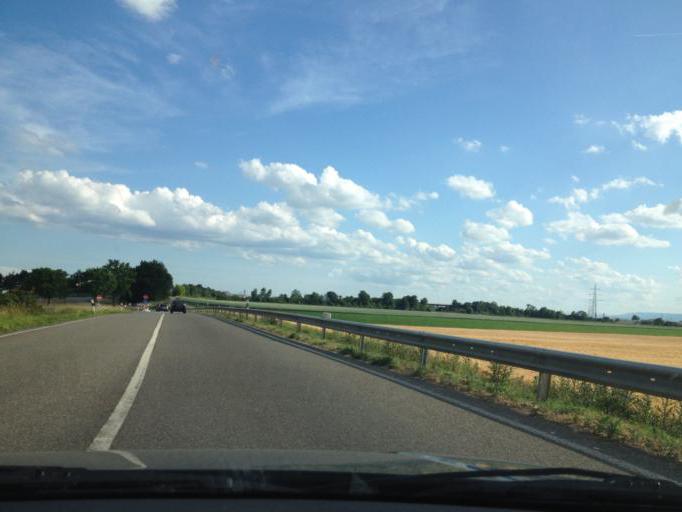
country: DE
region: Rheinland-Pfalz
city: Frankenthal
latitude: 49.5136
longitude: 8.3550
